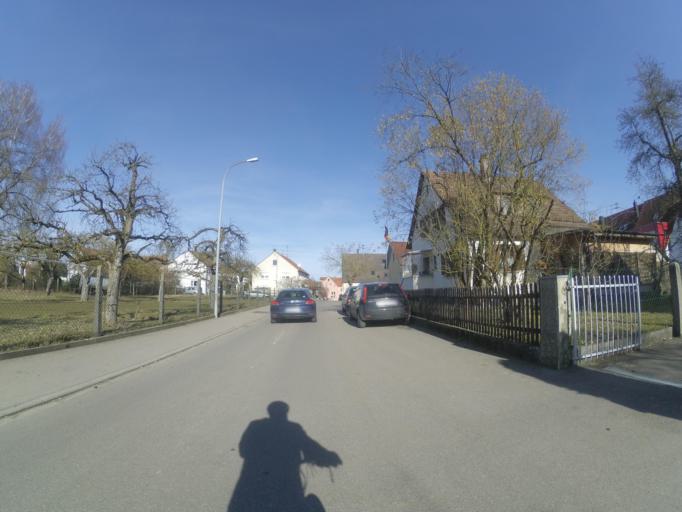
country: DE
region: Baden-Wuerttemberg
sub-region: Regierungsbezirk Stuttgart
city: Sontheim an der Brenz
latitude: 48.5519
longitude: 10.2890
